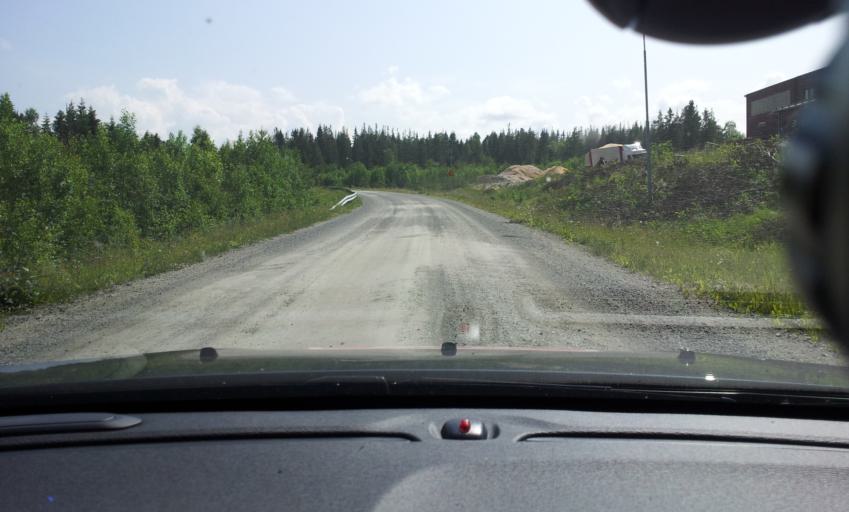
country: SE
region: Jaemtland
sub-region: Bergs Kommun
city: Hoverberg
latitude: 62.7961
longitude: 14.4769
